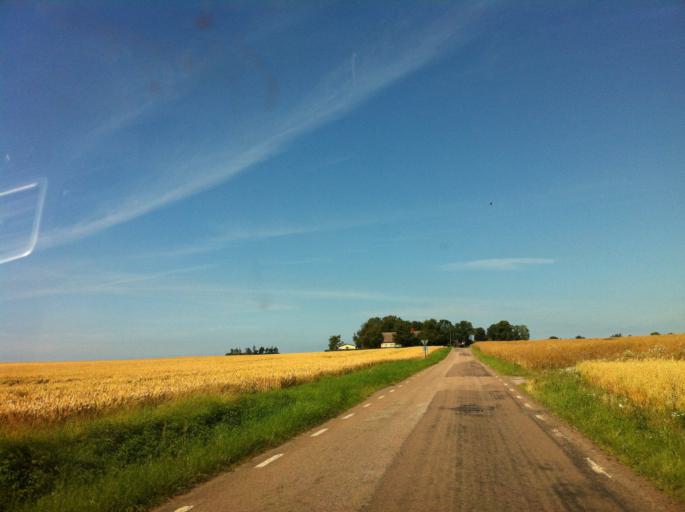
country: SE
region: Skane
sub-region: Helsingborg
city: Glumslov
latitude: 55.9387
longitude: 12.8486
